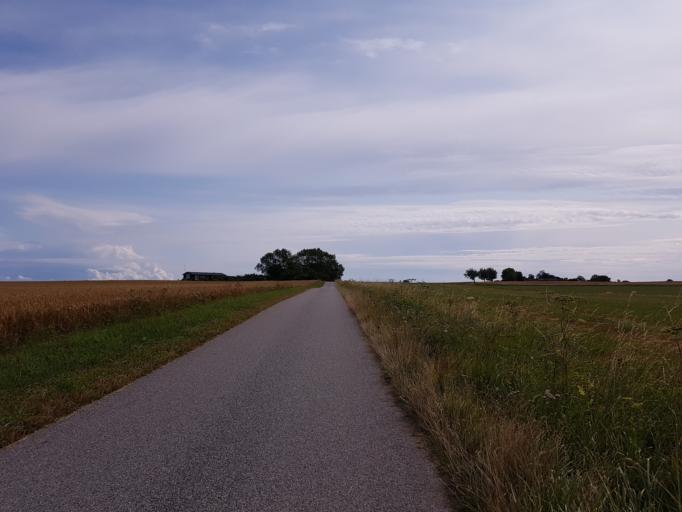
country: DK
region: Zealand
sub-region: Guldborgsund Kommune
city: Nykobing Falster
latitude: 54.5764
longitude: 11.9693
